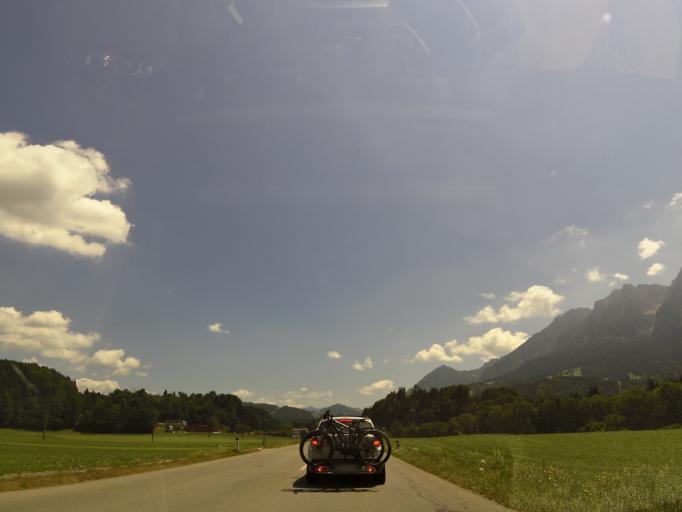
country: AT
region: Tyrol
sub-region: Politischer Bezirk Kufstein
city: Niederndorf
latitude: 47.6485
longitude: 12.2231
